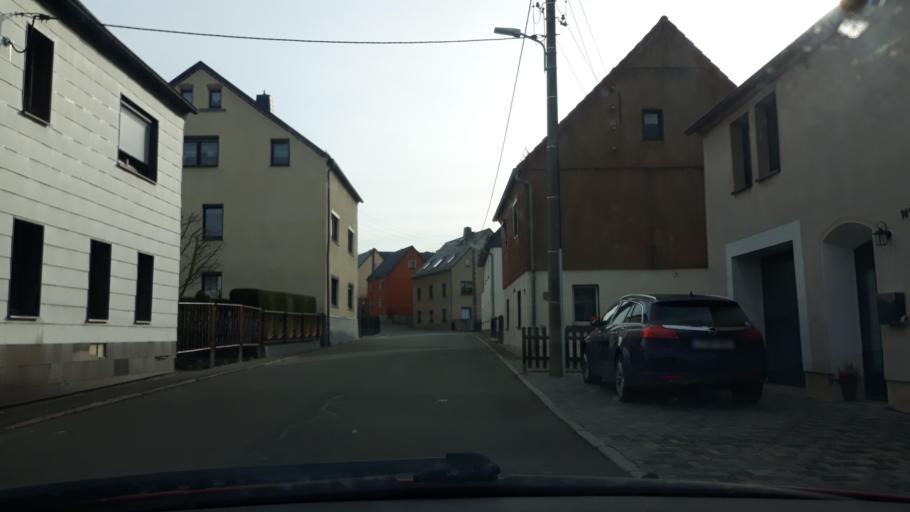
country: DE
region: Saxony
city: Reinsdorf
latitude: 50.6825
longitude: 12.5589
